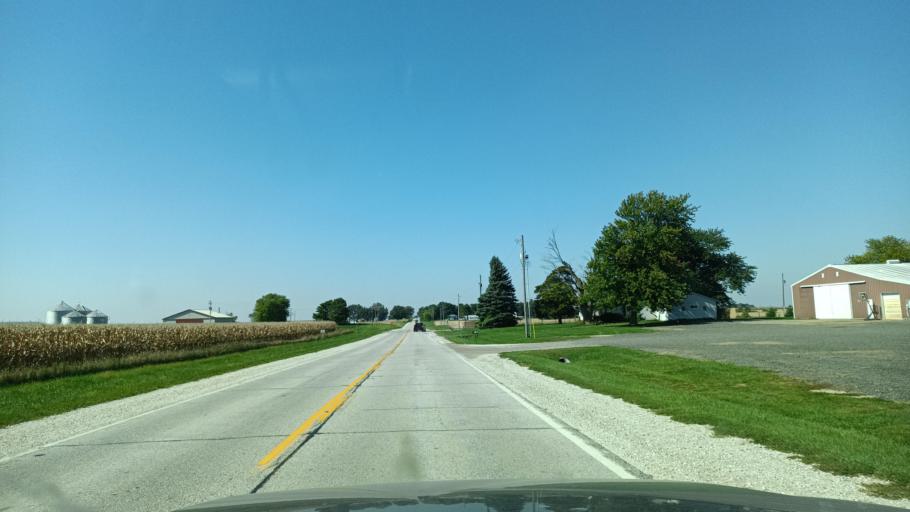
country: US
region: Illinois
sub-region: Warren County
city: Monmouth
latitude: 40.9139
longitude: -90.6779
